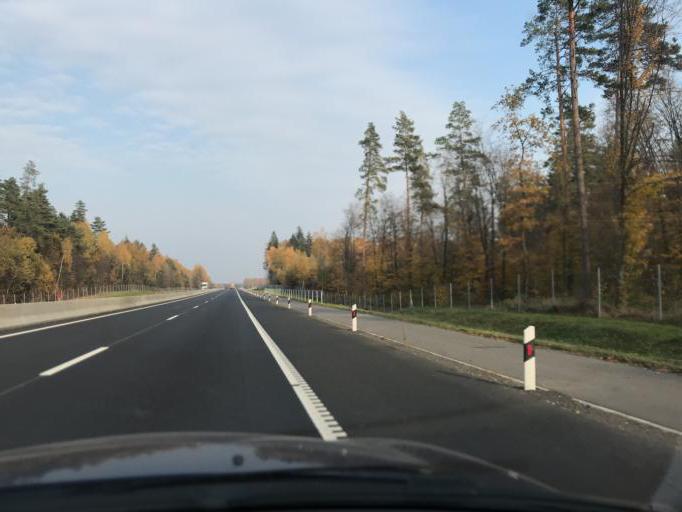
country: BY
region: Grodnenskaya
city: Shchuchin
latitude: 53.6718
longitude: 24.8322
